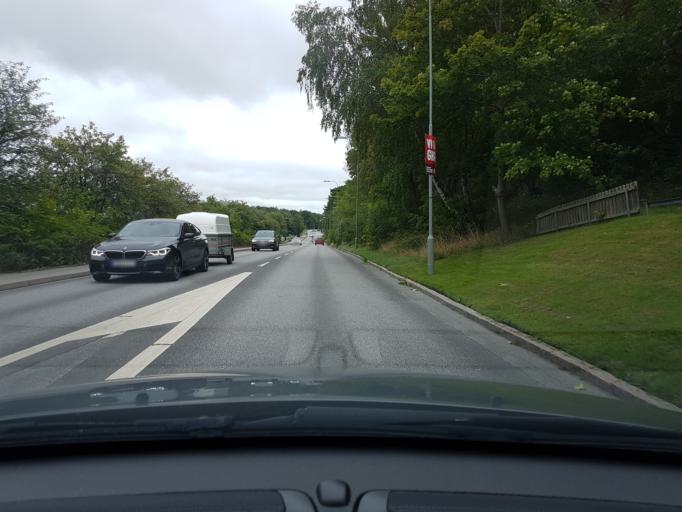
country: SE
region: Vaestra Goetaland
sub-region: Goteborg
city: Majorna
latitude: 57.6431
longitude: 11.8949
